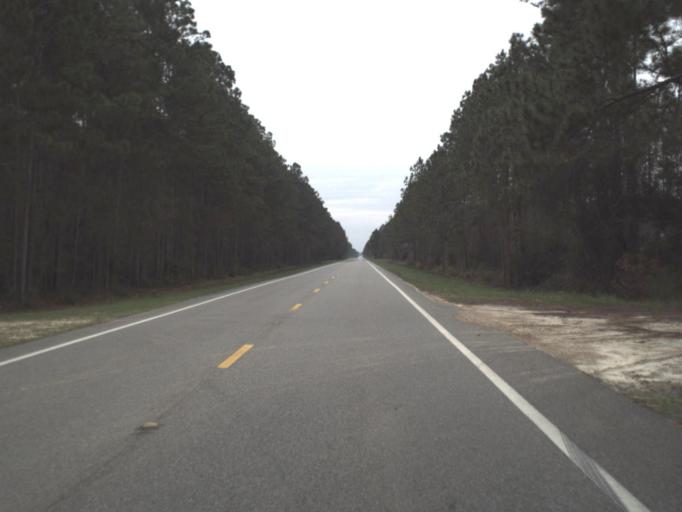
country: US
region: Florida
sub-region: Gulf County
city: Port Saint Joe
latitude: 29.9347
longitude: -85.1910
